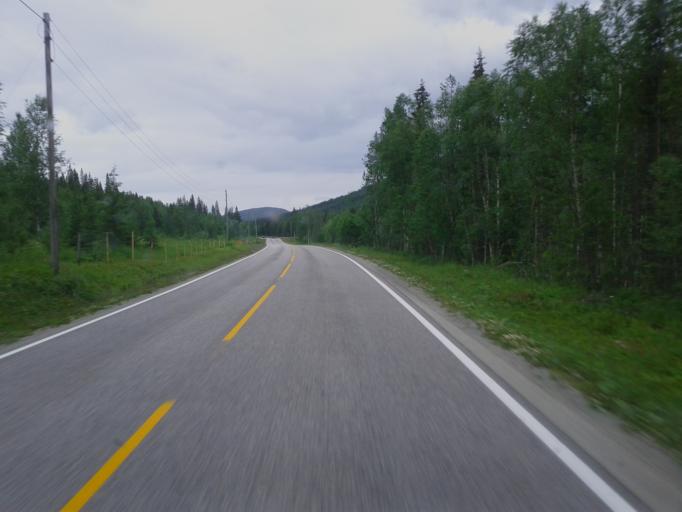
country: NO
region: Nord-Trondelag
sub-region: Namsskogan
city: Namsskogan
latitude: 64.8857
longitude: 13.0720
